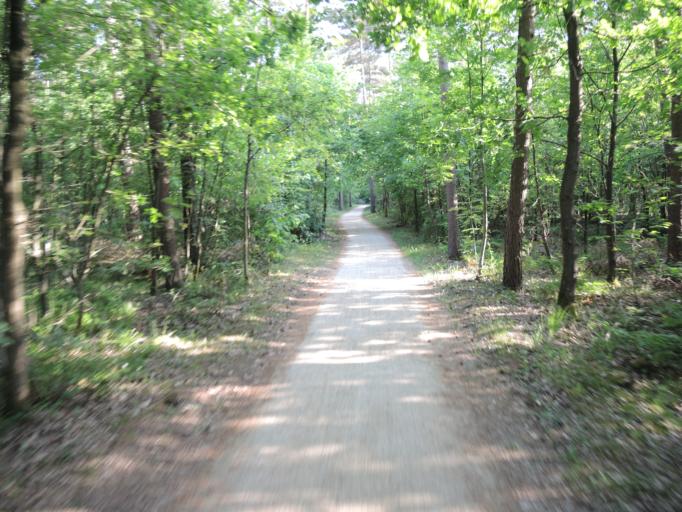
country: BE
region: Flanders
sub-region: Provincie Antwerpen
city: Lille
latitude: 51.2815
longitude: 4.8330
